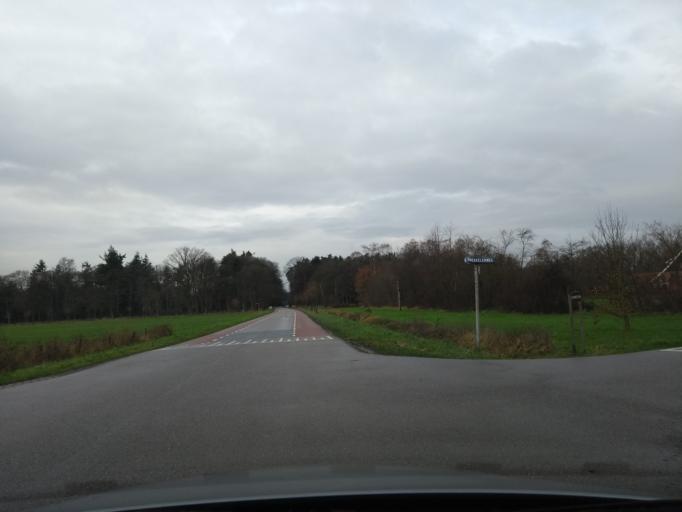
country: NL
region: Overijssel
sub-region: Gemeente Hengelo
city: Hengelo
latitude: 52.2229
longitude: 6.8293
